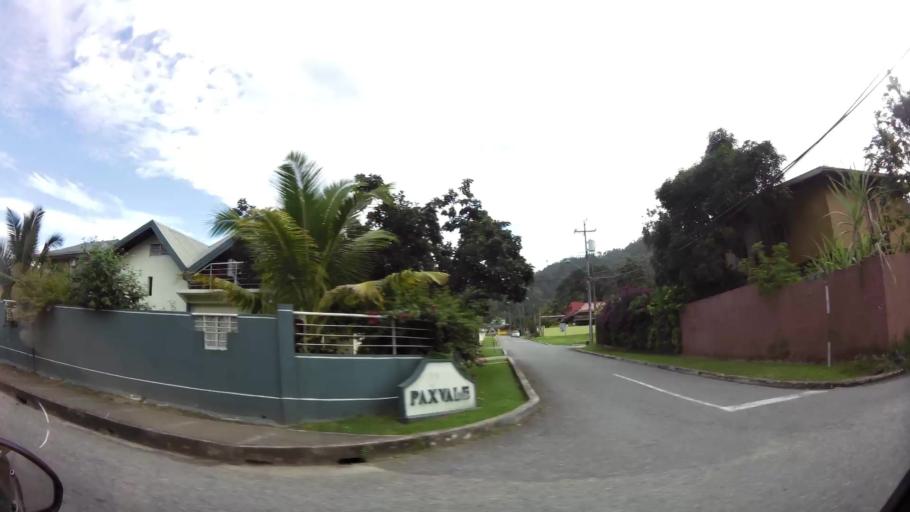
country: TT
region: San Juan/Laventille
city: Laventille
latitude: 10.7068
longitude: -61.4616
